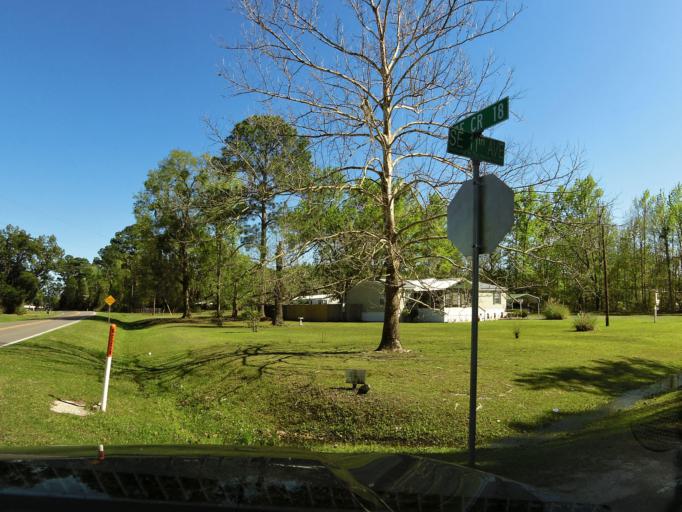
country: US
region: Florida
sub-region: Clay County
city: Keystone Heights
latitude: 29.8428
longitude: -82.0699
